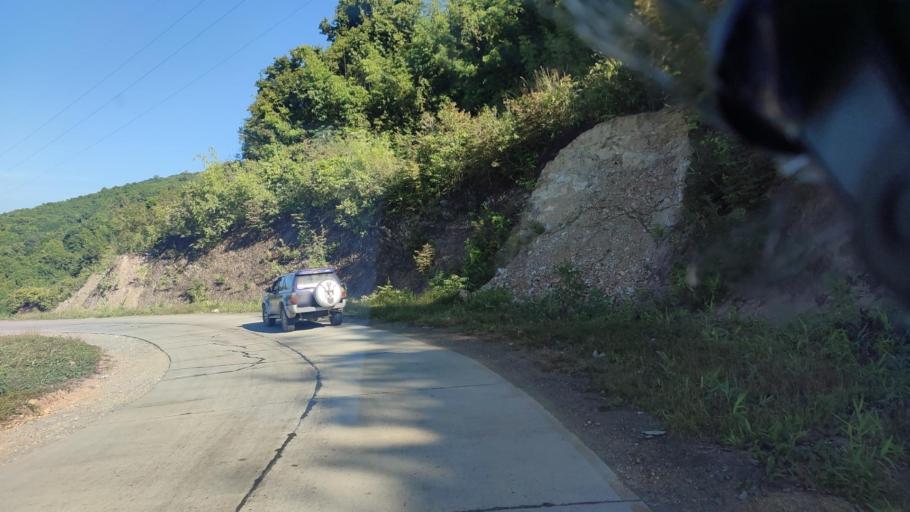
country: MM
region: Rakhine
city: Sittwe
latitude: 19.9309
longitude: 93.7636
